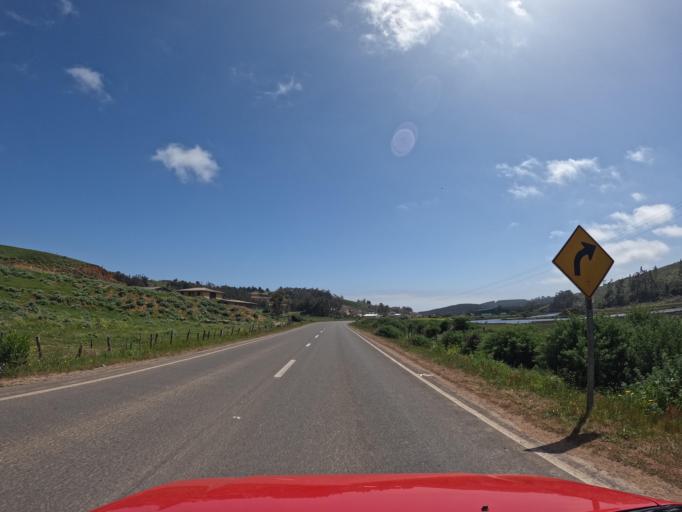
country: CL
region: O'Higgins
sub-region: Provincia de Colchagua
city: Santa Cruz
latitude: -34.6498
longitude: -72.0286
